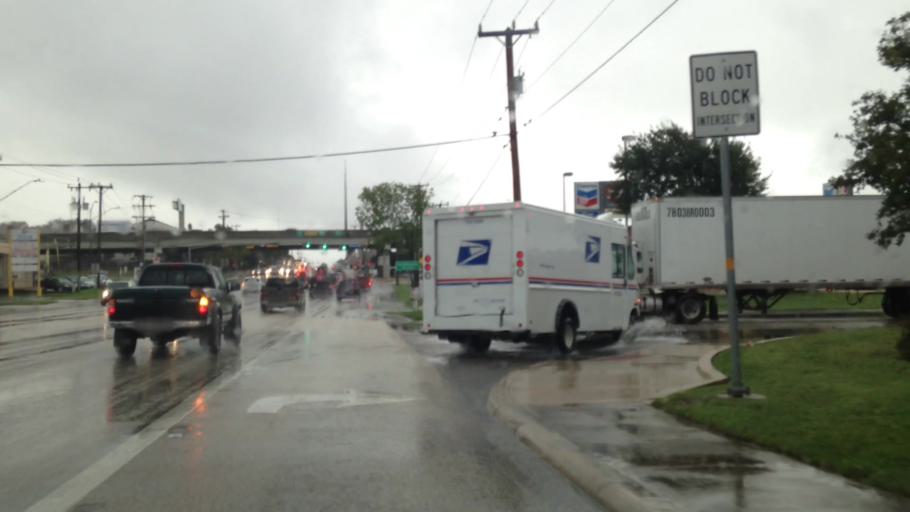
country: US
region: Texas
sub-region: Bexar County
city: Windcrest
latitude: 29.5341
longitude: -98.4109
